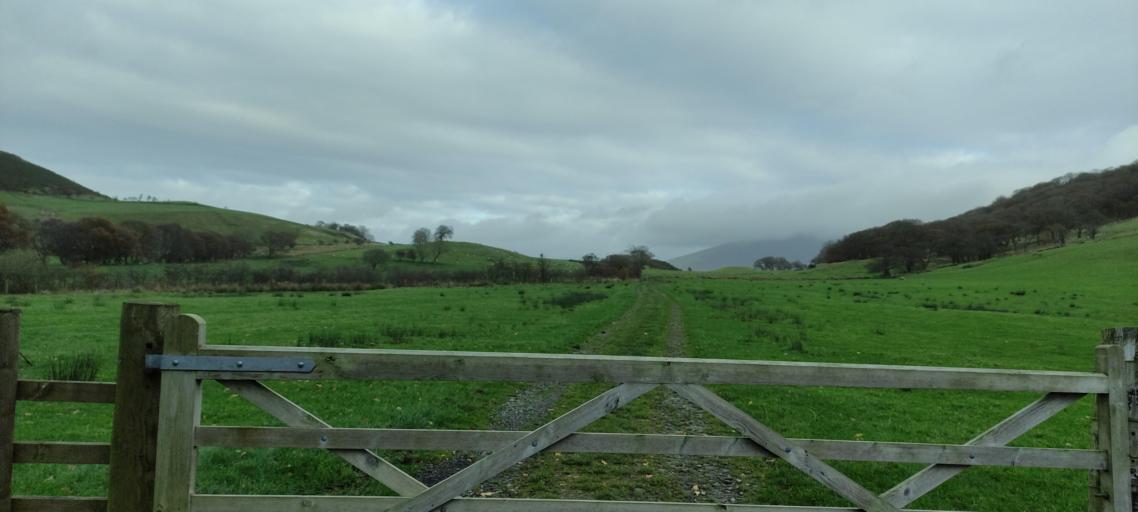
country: GB
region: England
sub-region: Cumbria
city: Cockermouth
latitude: 54.6481
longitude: -3.2422
